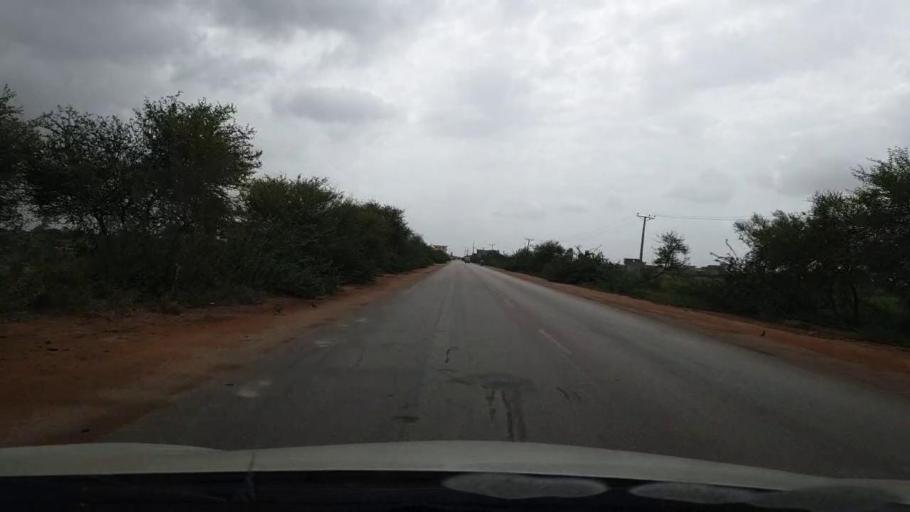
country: PK
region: Sindh
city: Mirpur Batoro
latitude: 24.6169
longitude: 68.2899
